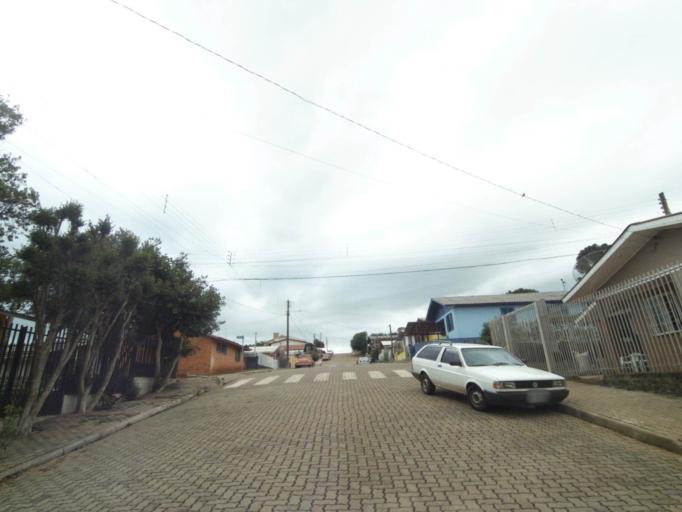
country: BR
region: Rio Grande do Sul
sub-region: Lagoa Vermelha
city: Lagoa Vermelha
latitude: -28.2013
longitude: -51.5259
